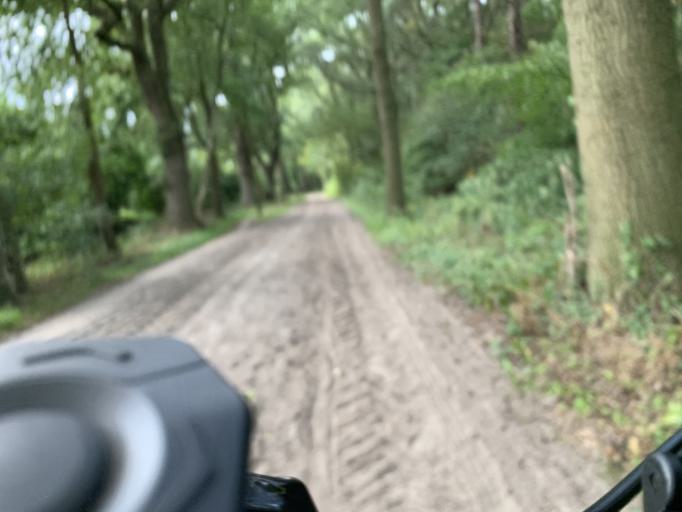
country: DE
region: Lower Saxony
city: Westerstede
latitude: 53.2349
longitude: 7.9165
